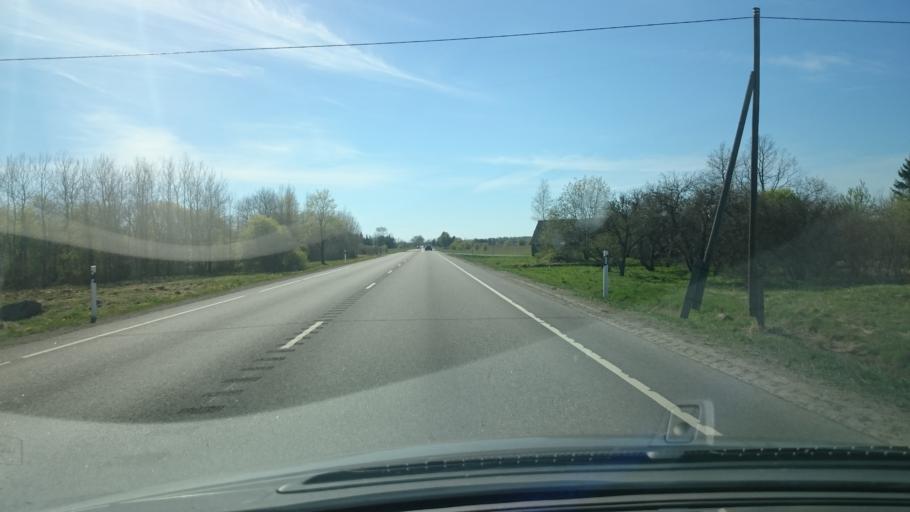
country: EE
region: Ida-Virumaa
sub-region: Kohtla-Jaerve linn
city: Kohtla-Jarve
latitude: 59.4211
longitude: 27.2100
